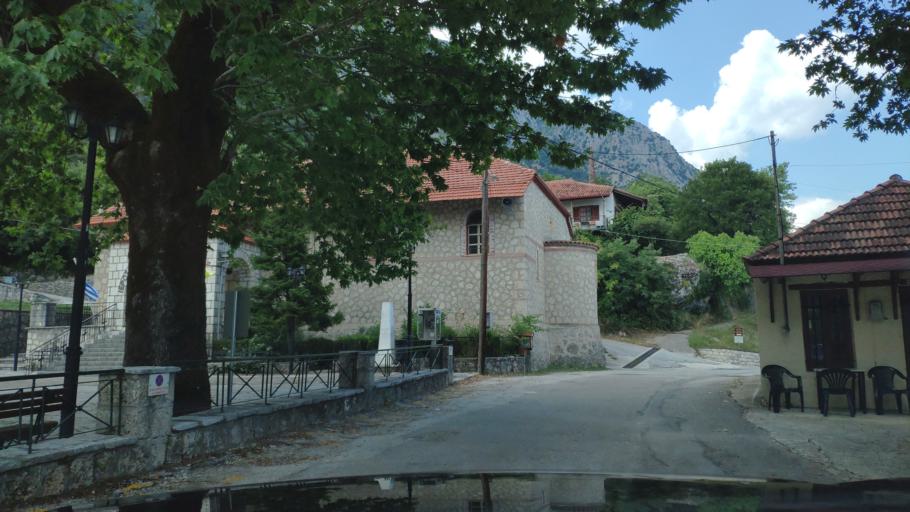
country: GR
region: Epirus
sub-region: Nomos Artas
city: Agios Dimitrios
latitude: 39.4167
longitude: 21.0099
